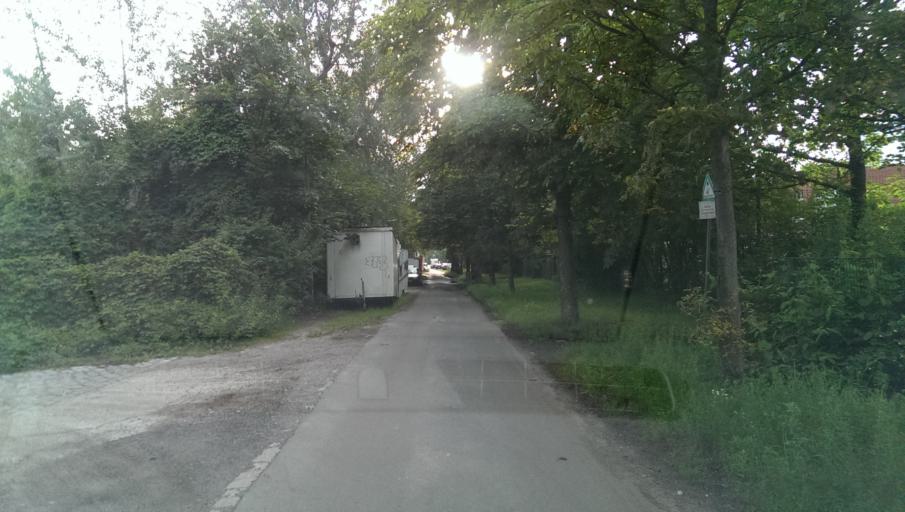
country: DE
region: Berlin
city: Lichterfelde
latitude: 52.4106
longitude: 13.3193
